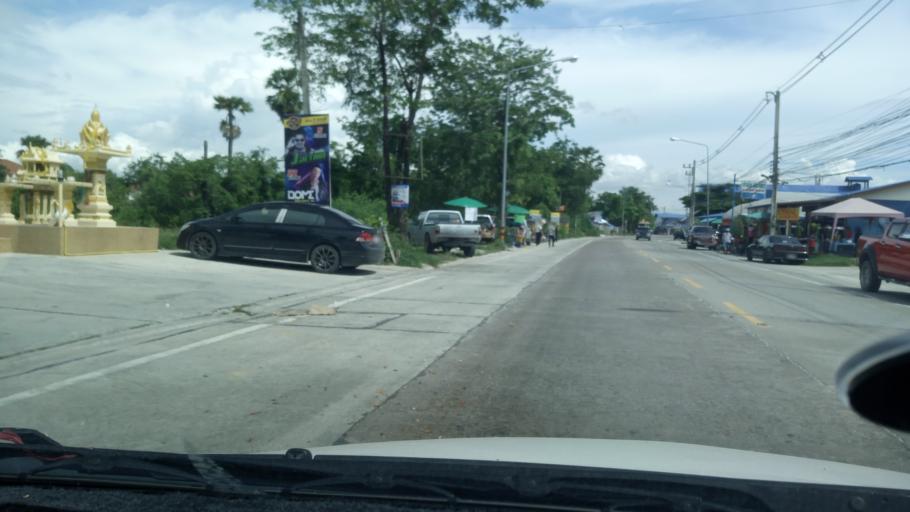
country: TH
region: Chon Buri
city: Chon Buri
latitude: 13.4117
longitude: 101.0285
